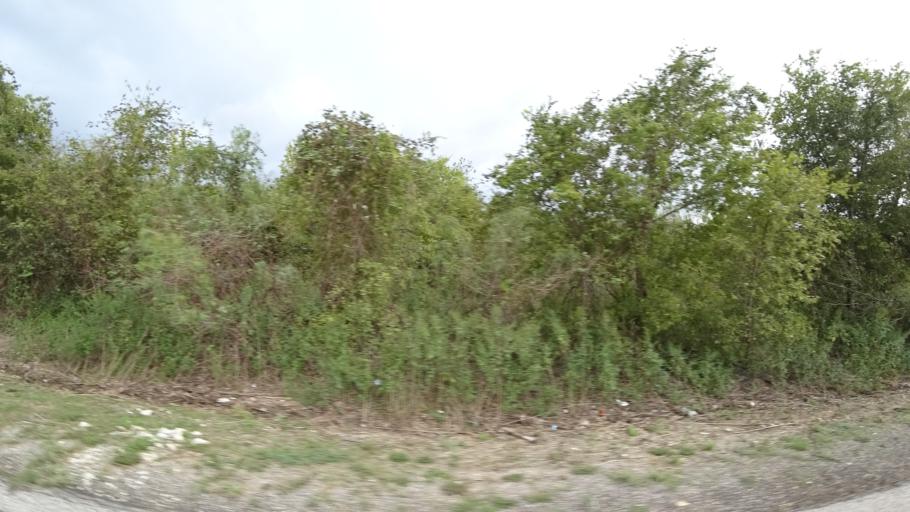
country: US
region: Texas
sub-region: Travis County
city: Onion Creek
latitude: 30.1582
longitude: -97.7328
